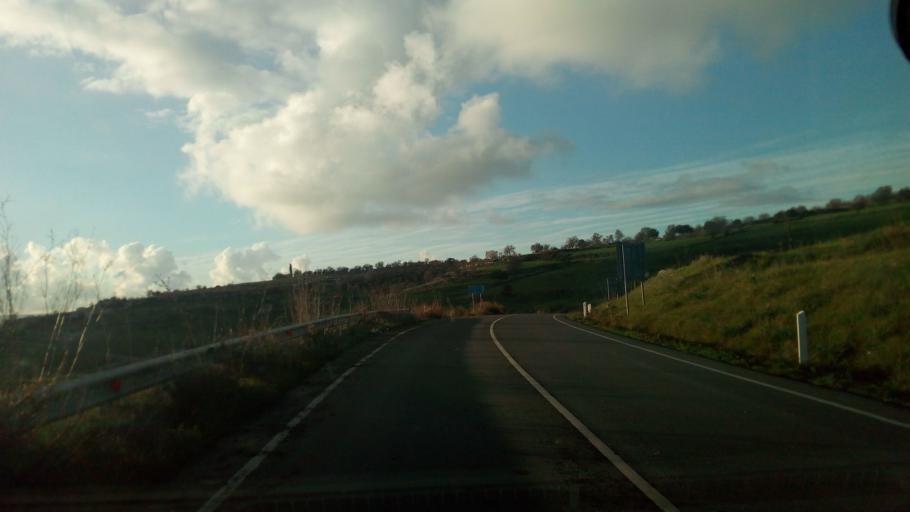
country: CY
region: Pafos
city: Mesogi
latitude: 34.9181
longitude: 32.5378
